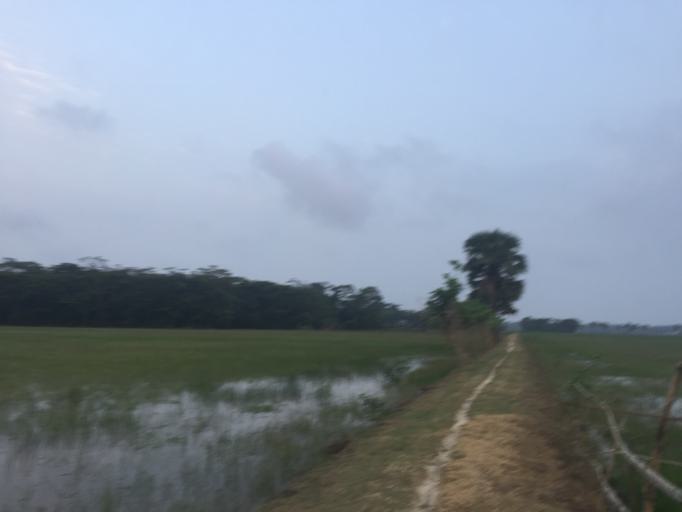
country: BD
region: Barisal
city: Mathba
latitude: 22.1925
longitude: 89.9350
